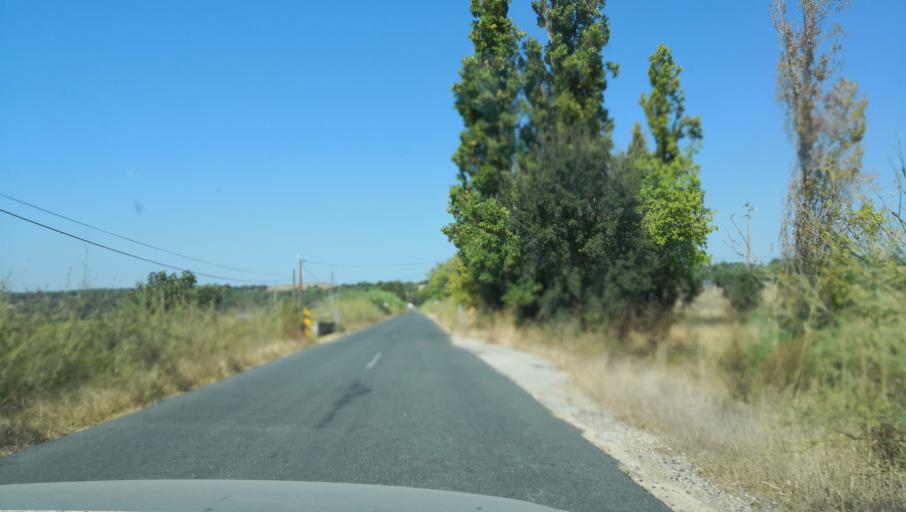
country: PT
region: Setubal
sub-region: Alcacer do Sal
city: Alcacer do Sal
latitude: 38.2851
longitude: -8.4019
